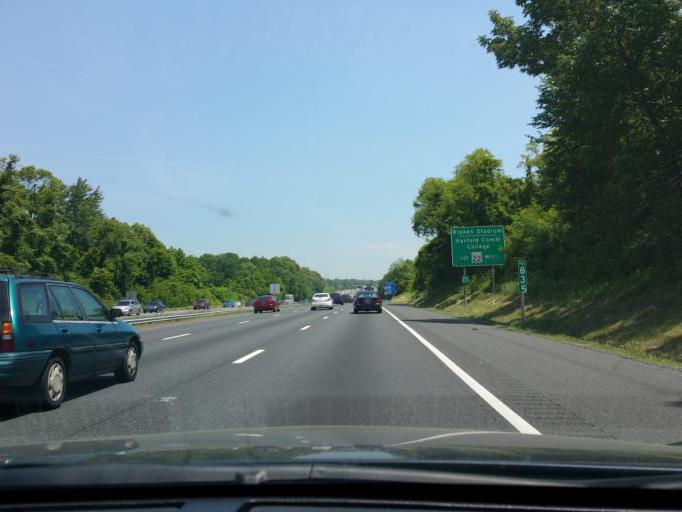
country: US
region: Maryland
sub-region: Harford County
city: Aberdeen
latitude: 39.5145
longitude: -76.2051
